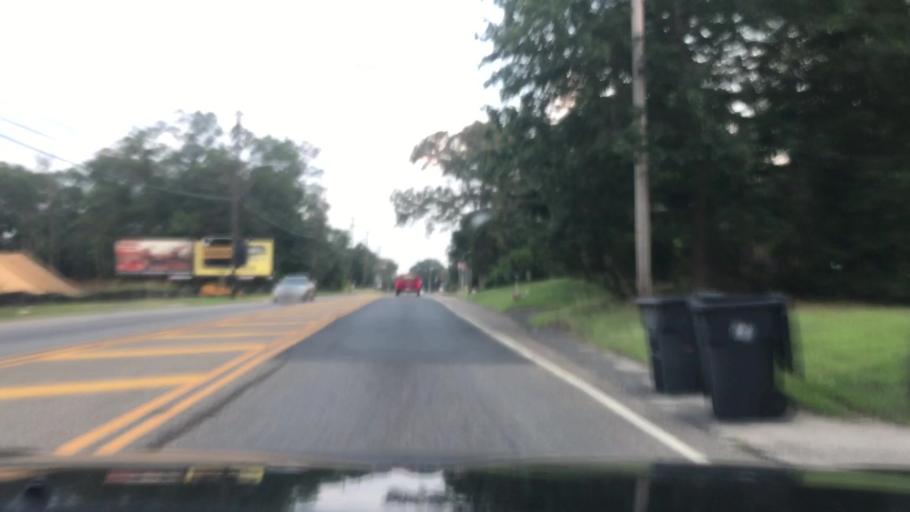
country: US
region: New Jersey
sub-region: Ocean County
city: Silver Ridge
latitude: 39.9996
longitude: -74.2123
